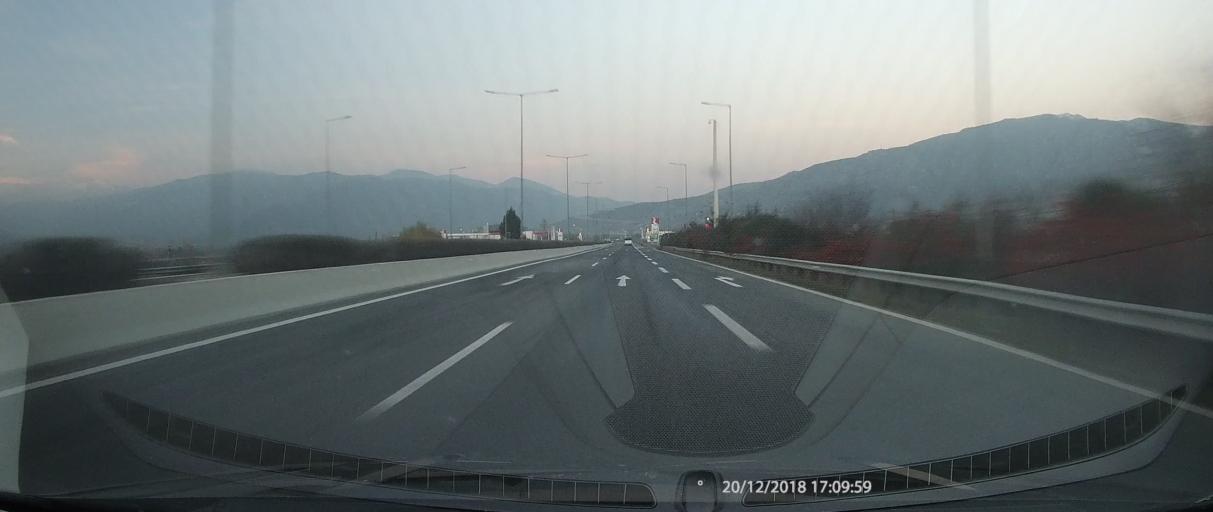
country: GR
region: Thessaly
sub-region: Nomos Larisis
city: Makrychori
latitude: 39.8115
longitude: 22.5064
